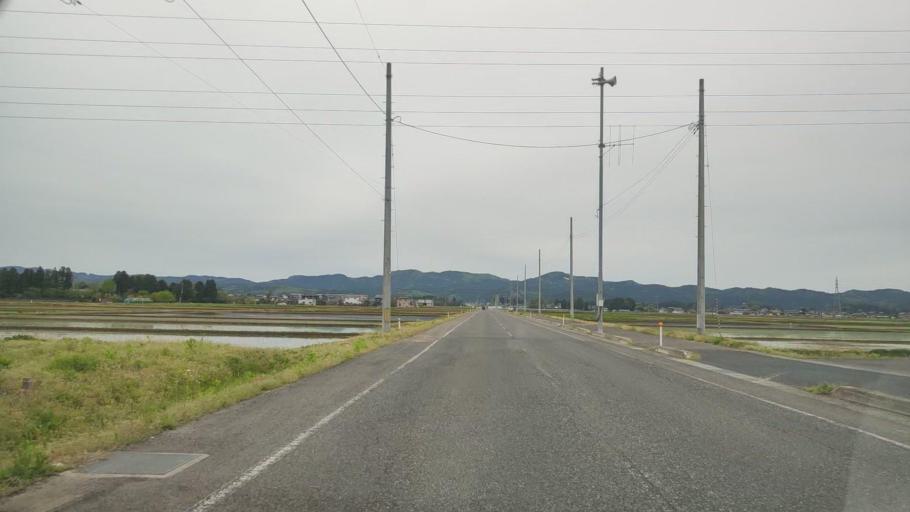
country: JP
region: Niigata
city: Gosen
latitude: 37.7292
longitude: 139.1749
